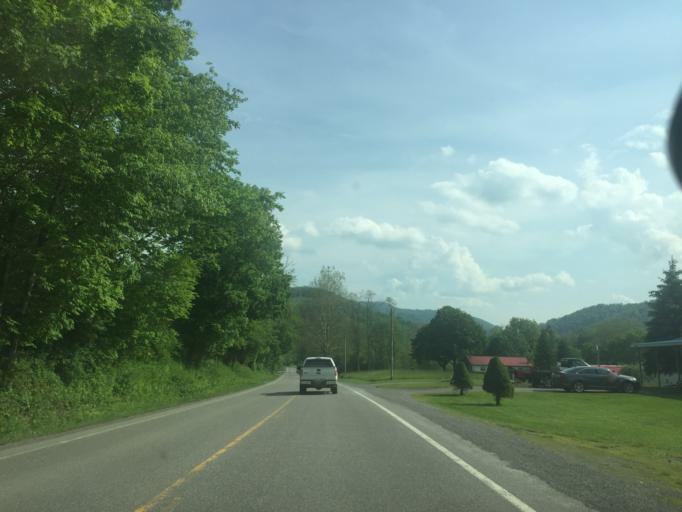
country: US
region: West Virginia
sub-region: Tucker County
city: Parsons
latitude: 38.9393
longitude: -79.5192
